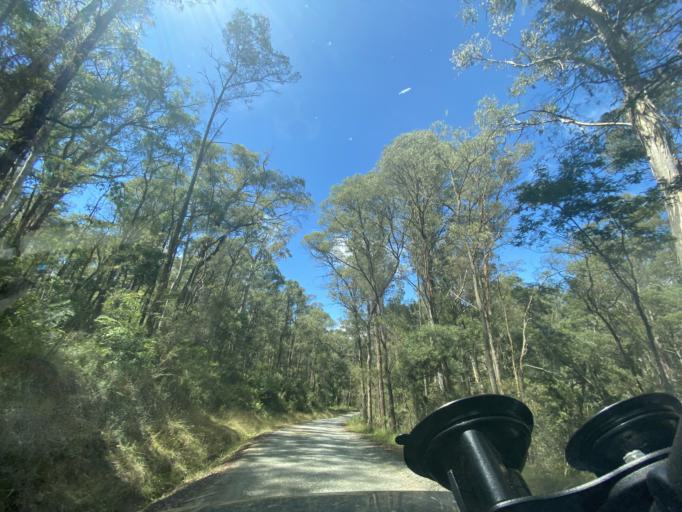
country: AU
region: Victoria
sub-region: Yarra Ranges
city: Millgrove
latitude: -37.5232
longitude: 146.0137
